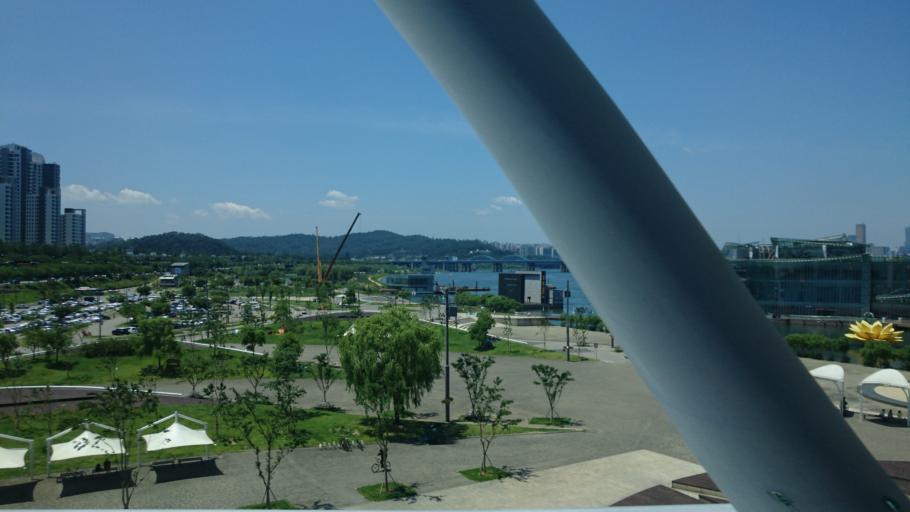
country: KR
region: Seoul
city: Seoul
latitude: 37.5130
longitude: 126.9972
